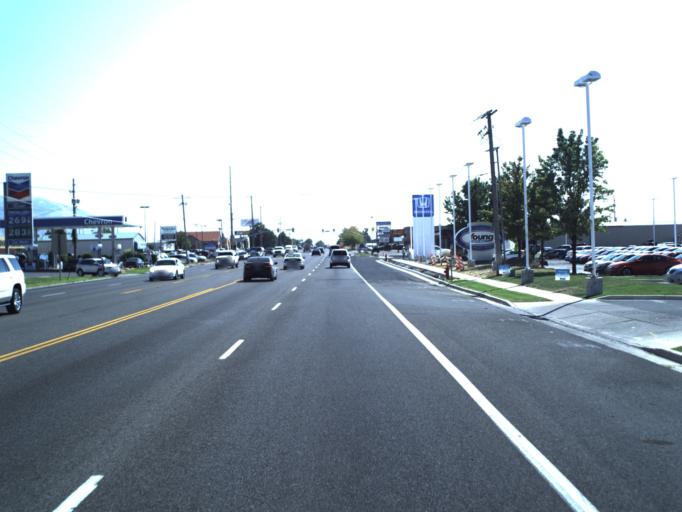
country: US
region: Utah
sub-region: Cache County
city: North Logan
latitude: 41.7674
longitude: -111.8343
